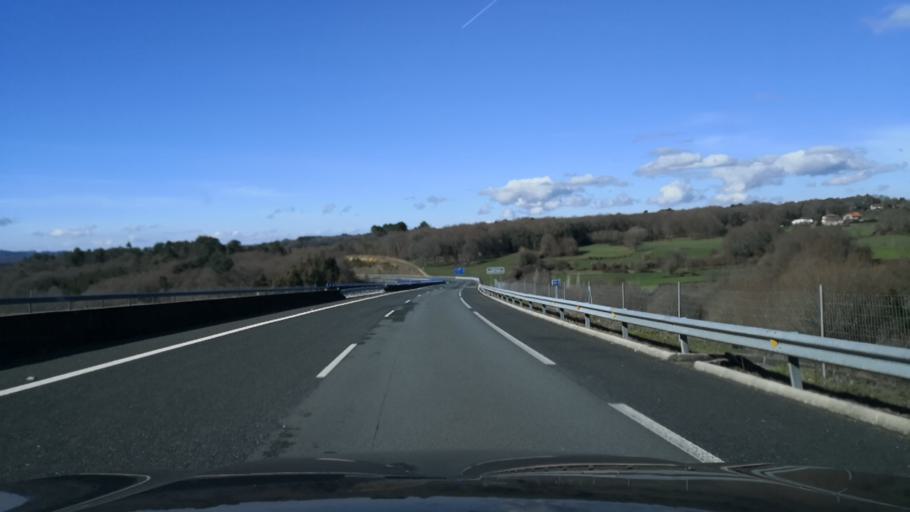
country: ES
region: Galicia
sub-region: Provincia de Pontevedra
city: Lalin
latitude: 42.6271
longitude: -8.1169
